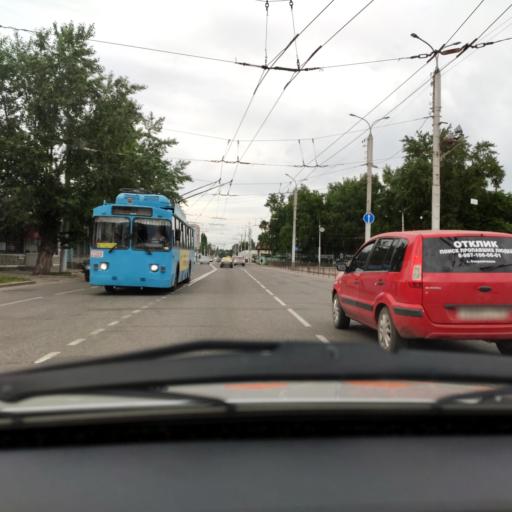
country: RU
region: Bashkortostan
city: Sterlitamak
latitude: 53.6143
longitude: 55.9561
